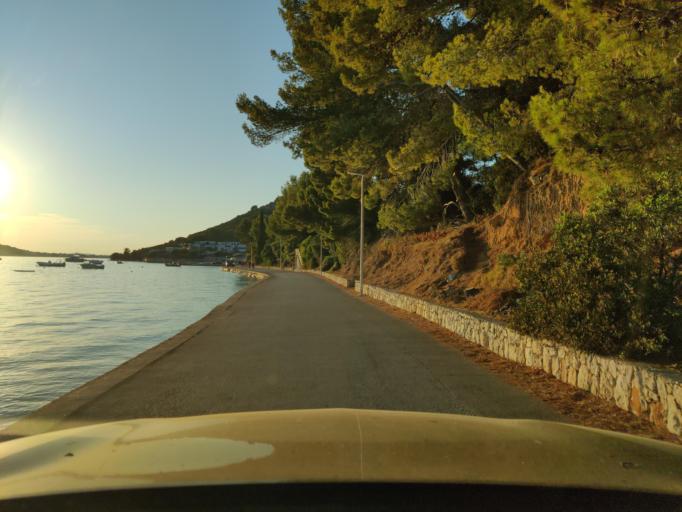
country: HR
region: Sibensko-Kniniska
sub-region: Grad Sibenik
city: Tisno
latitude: 43.8067
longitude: 15.6296
